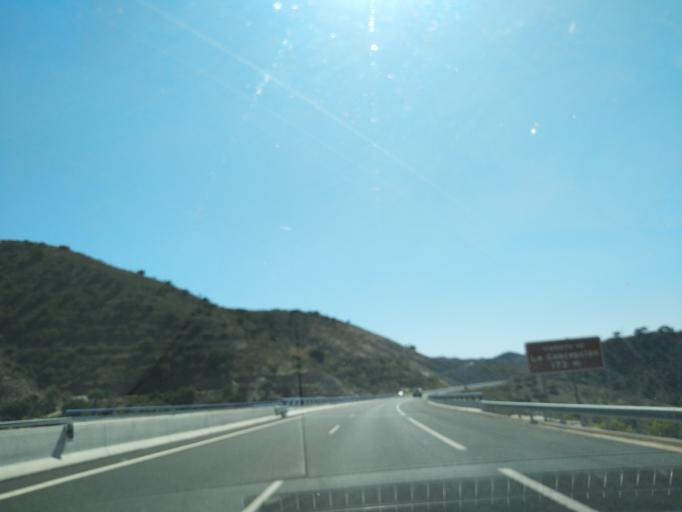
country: ES
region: Andalusia
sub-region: Provincia de Malaga
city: Almogia
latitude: 36.8320
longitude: -4.4714
